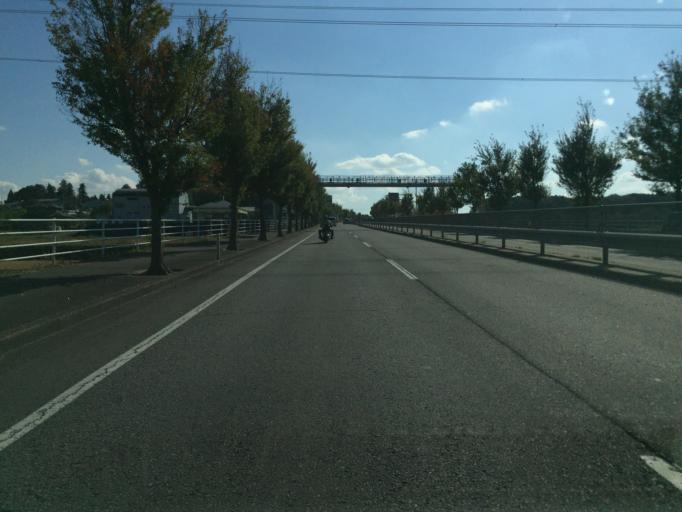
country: JP
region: Fukushima
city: Nihommatsu
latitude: 37.6469
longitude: 140.4872
